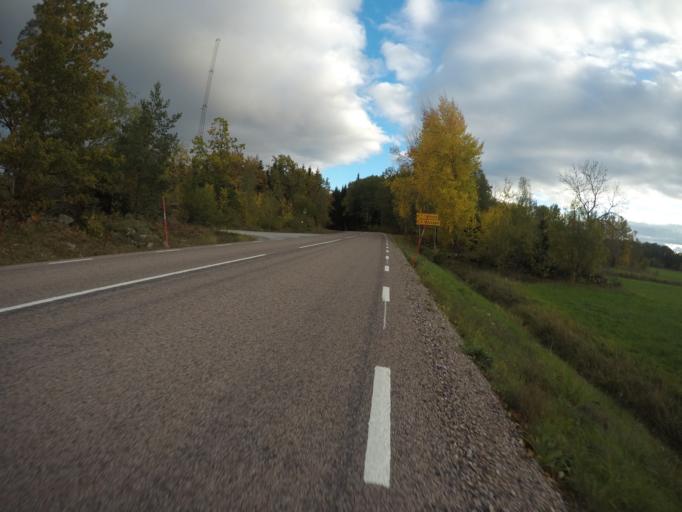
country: SE
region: Vaestmanland
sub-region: Arboga Kommun
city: Tyringe
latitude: 59.3122
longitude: 15.9864
